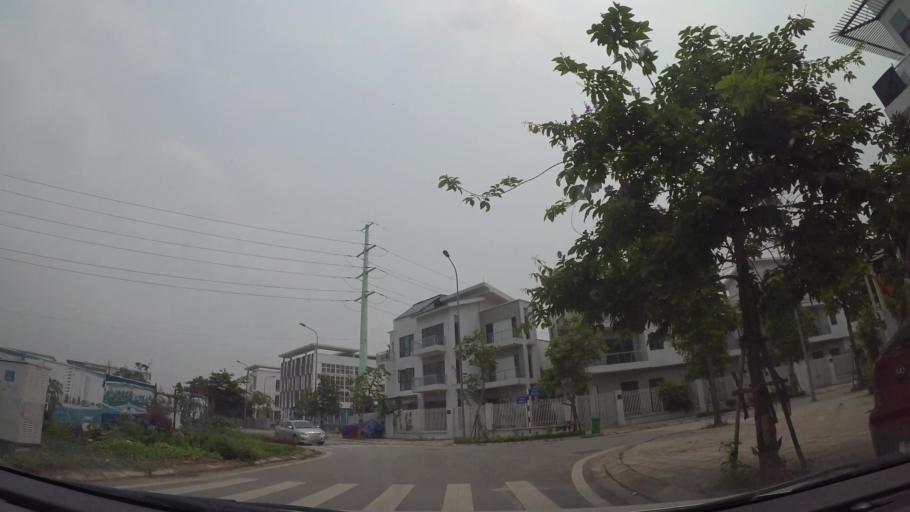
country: VN
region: Ha Noi
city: Cau Dien
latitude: 21.0287
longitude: 105.7446
